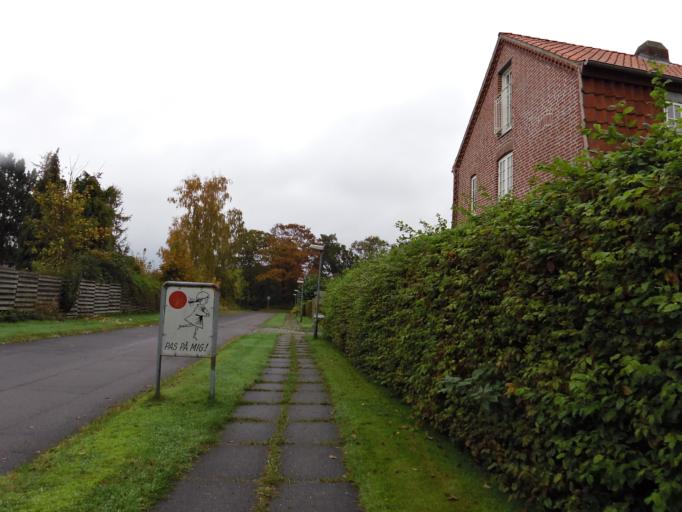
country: DK
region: Central Jutland
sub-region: Arhus Kommune
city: Stavtrup
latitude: 56.1384
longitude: 10.1236
